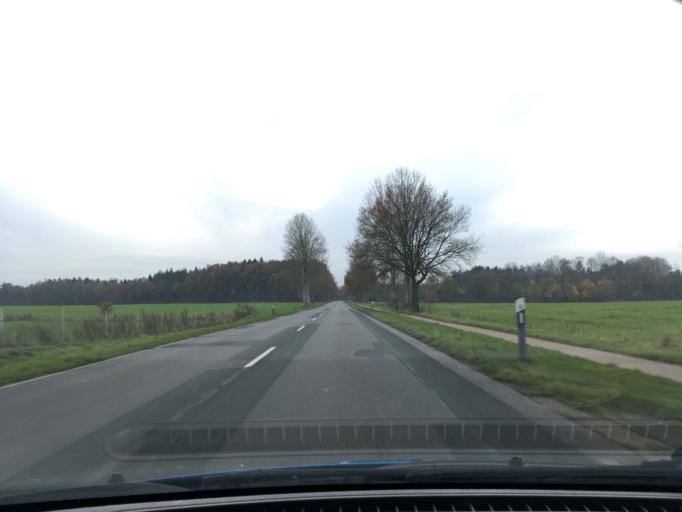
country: DE
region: Lower Saxony
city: Embsen
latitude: 53.2068
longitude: 10.3641
